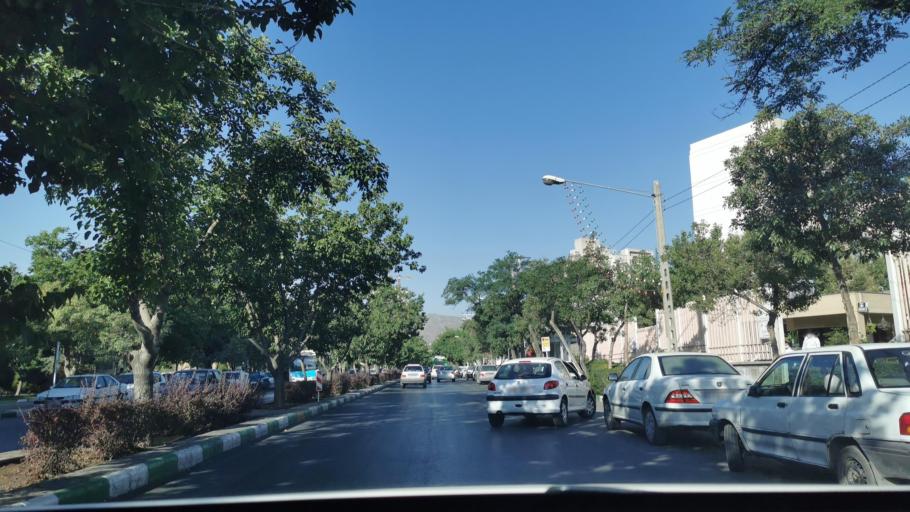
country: IR
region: Razavi Khorasan
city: Mashhad
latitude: 36.3188
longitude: 59.5238
